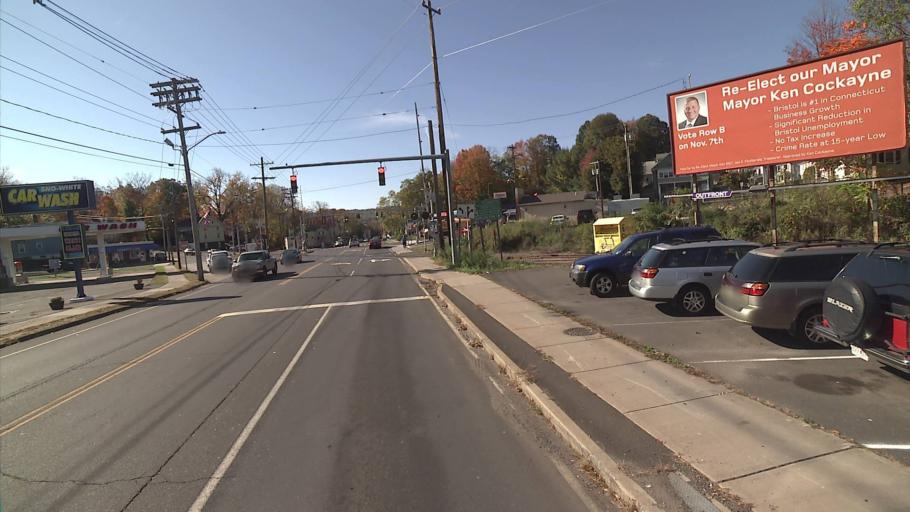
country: US
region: Connecticut
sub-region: Hartford County
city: Bristol
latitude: 41.6830
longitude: -72.9415
